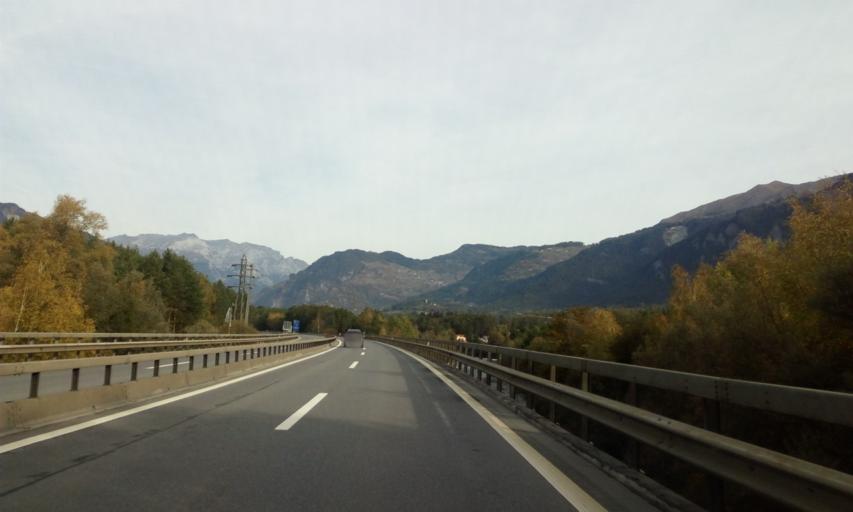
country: CH
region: Grisons
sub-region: Hinterrhein District
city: Thusis
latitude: 46.7078
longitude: 9.4490
